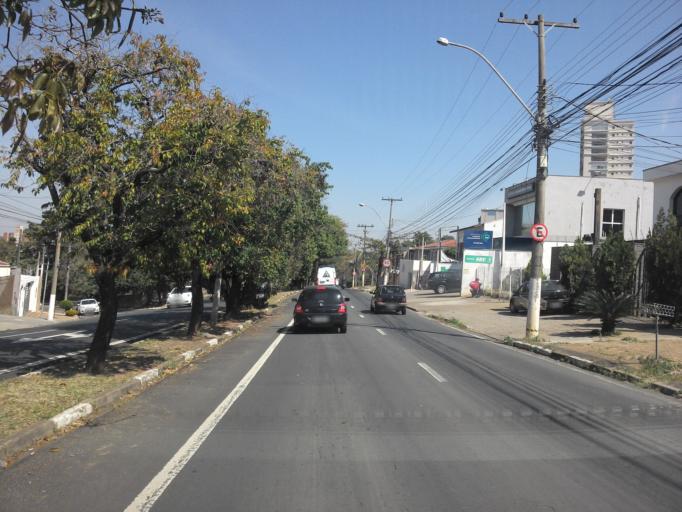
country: BR
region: Sao Paulo
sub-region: Campinas
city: Campinas
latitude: -22.8935
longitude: -47.0858
